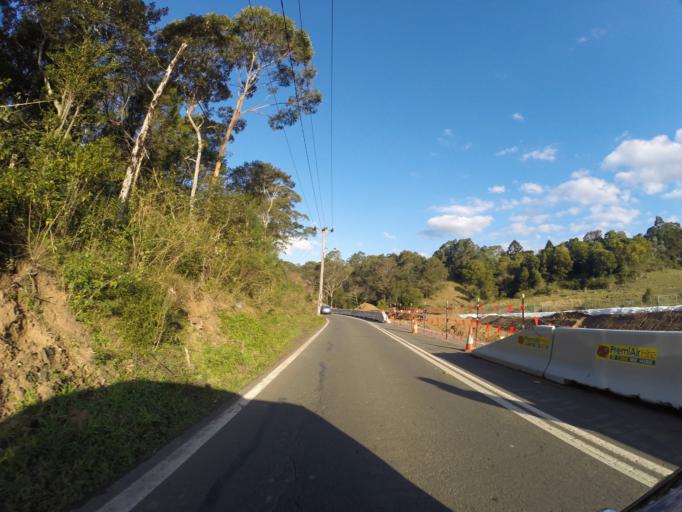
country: AU
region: New South Wales
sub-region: Wollongong
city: Cordeaux Heights
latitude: -34.4332
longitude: 150.8309
